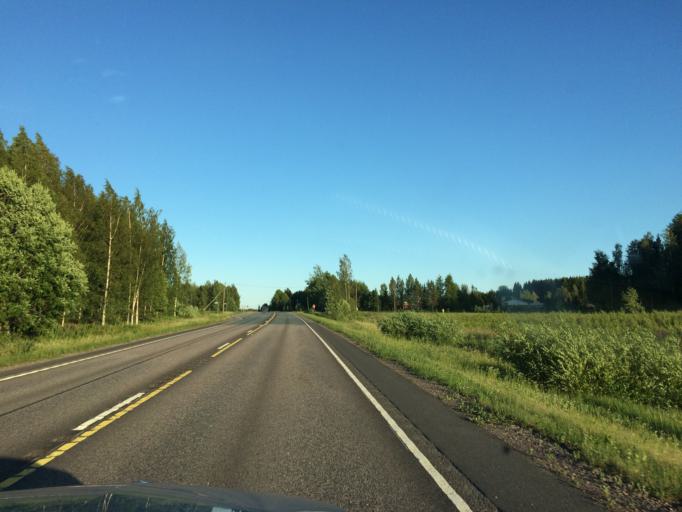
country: FI
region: Haeme
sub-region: Haemeenlinna
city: Tervakoski
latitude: 60.8100
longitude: 24.6485
